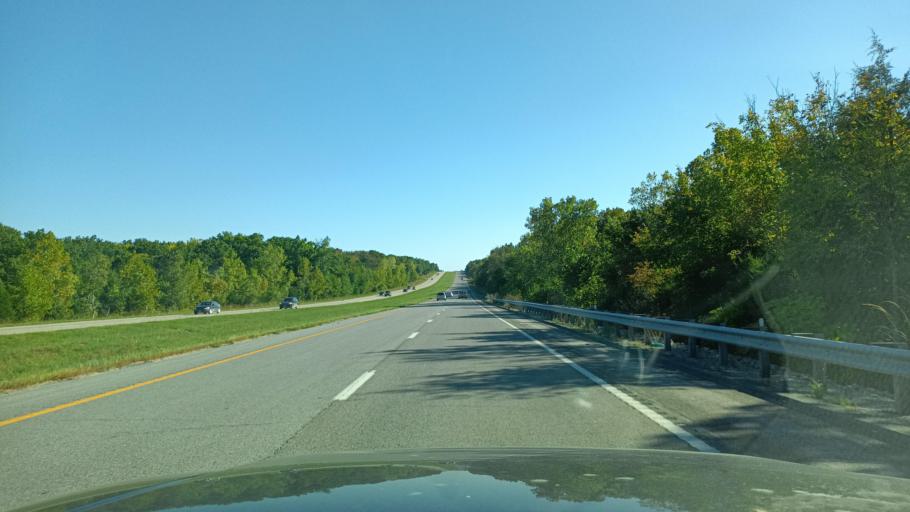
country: US
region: Missouri
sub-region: Boone County
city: Hallsville
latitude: 39.1057
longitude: -92.3293
